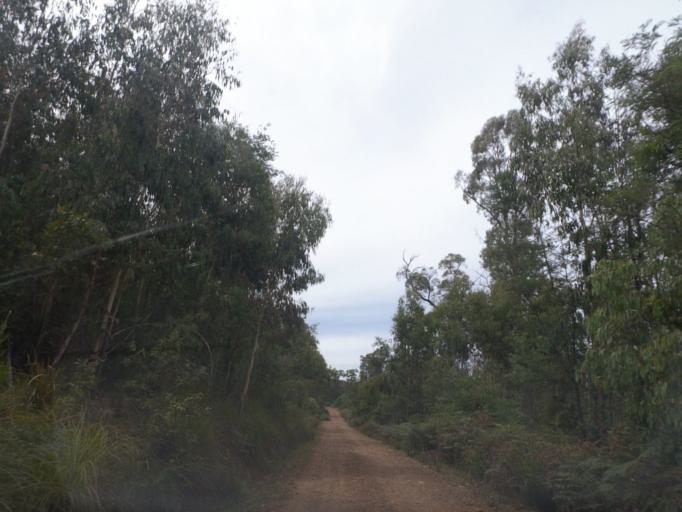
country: AU
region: Victoria
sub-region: Yarra Ranges
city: Healesville
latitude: -37.4336
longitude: 145.5775
